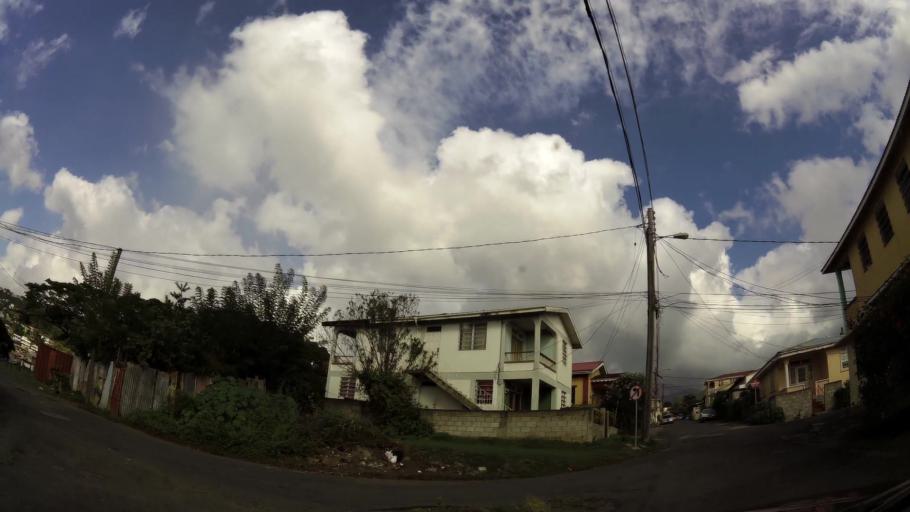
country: DM
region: Saint George
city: Roseau
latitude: 15.3048
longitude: -61.3877
